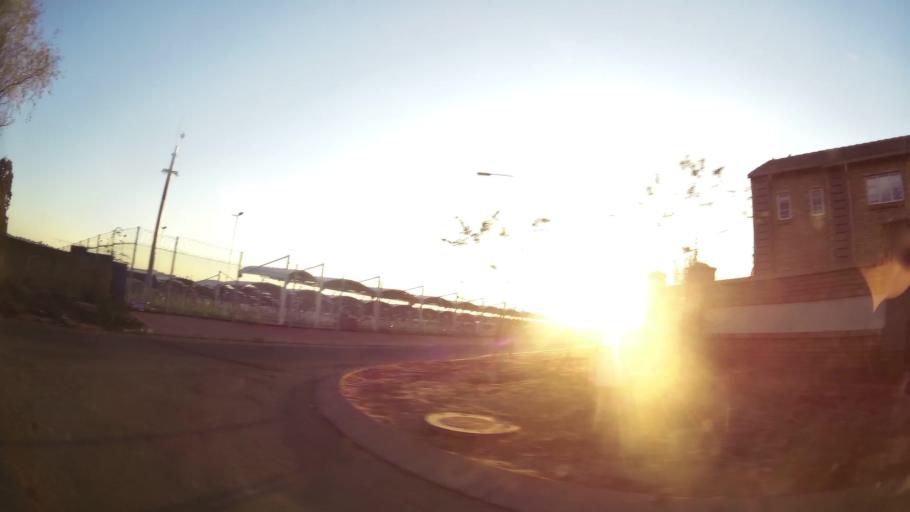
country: ZA
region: Gauteng
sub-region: City of Tshwane Metropolitan Municipality
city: Centurion
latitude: -25.8492
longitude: 28.1939
